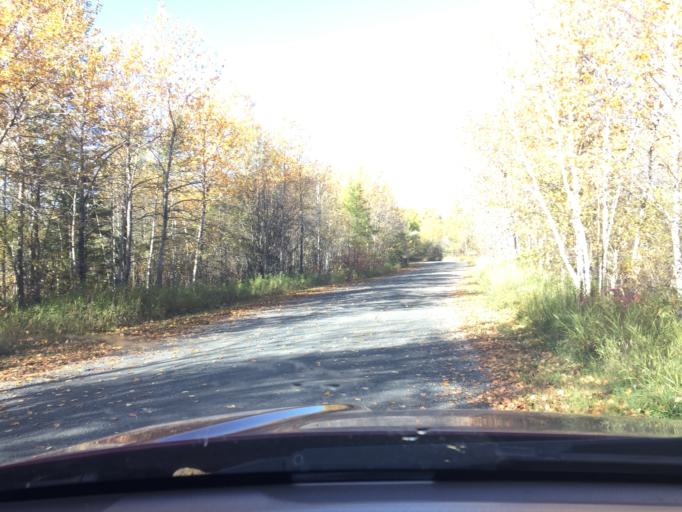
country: US
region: Minnesota
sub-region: Lake of the Woods County
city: Baudette
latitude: 48.2865
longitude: -94.5541
